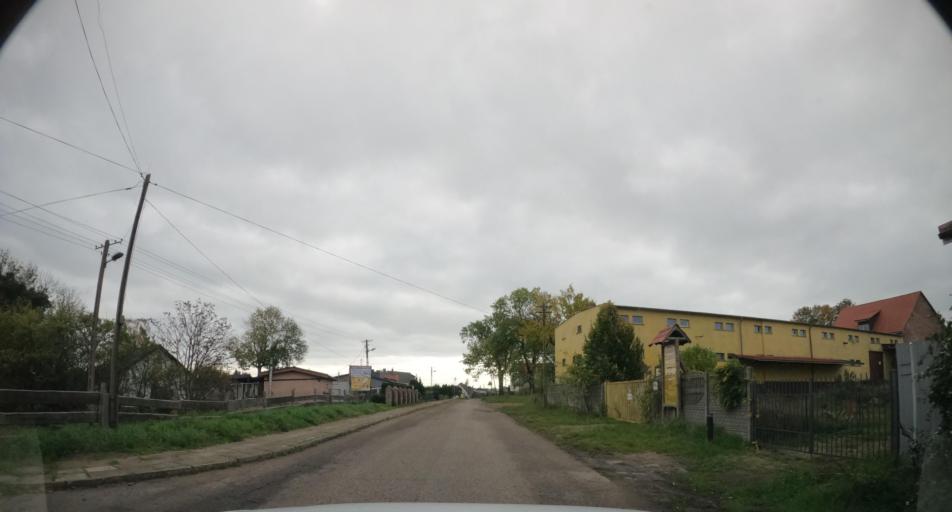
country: PL
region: West Pomeranian Voivodeship
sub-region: Powiat kamienski
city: Wolin
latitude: 53.8663
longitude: 14.5896
